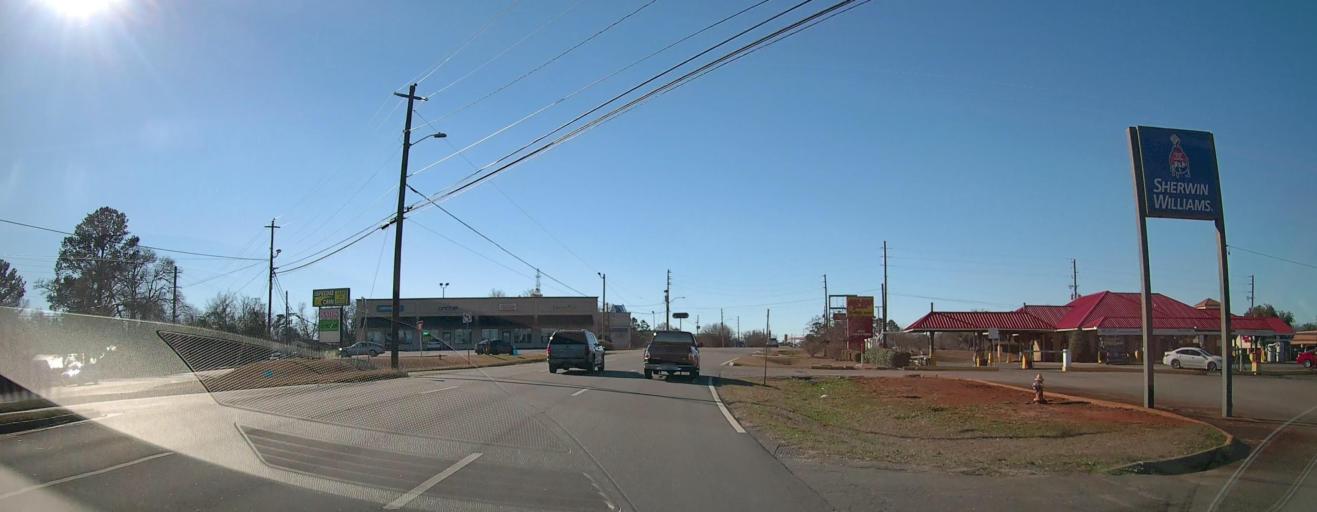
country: US
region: Georgia
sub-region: Sumter County
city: Americus
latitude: 32.0715
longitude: -84.2117
